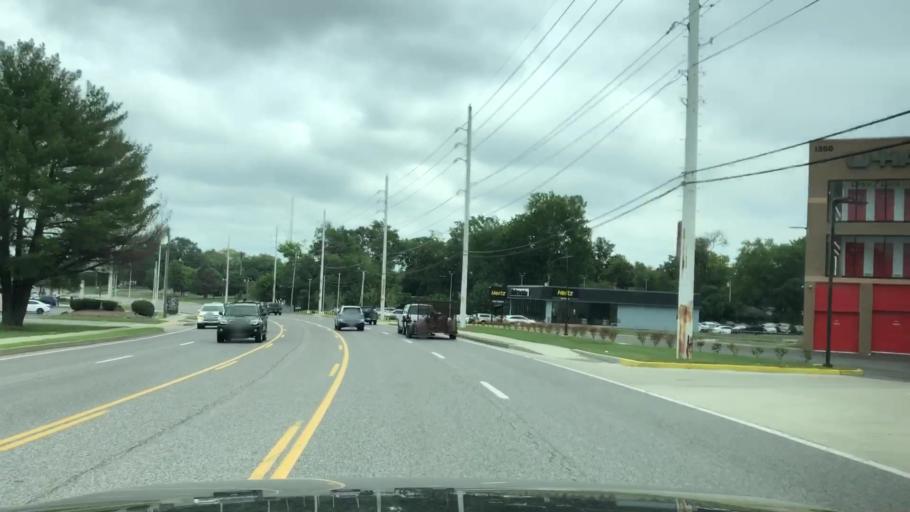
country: US
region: Missouri
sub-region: Saint Louis County
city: Florissant
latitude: 38.7980
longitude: -90.3214
